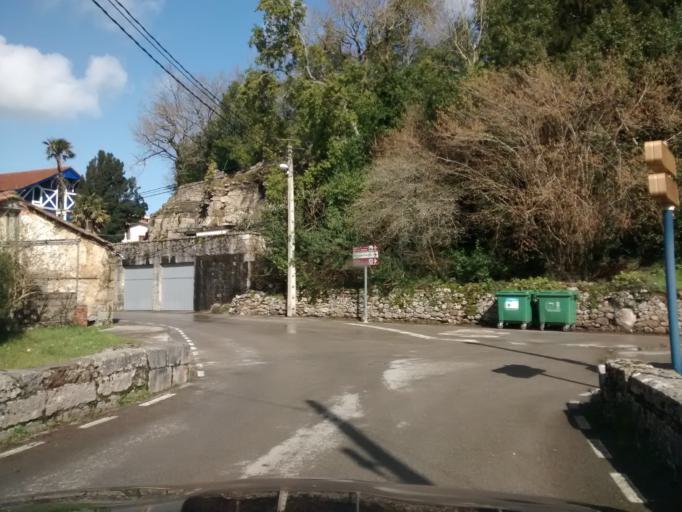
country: ES
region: Cantabria
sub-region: Provincia de Cantabria
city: Entrambasaguas
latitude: 43.3509
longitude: -3.7064
